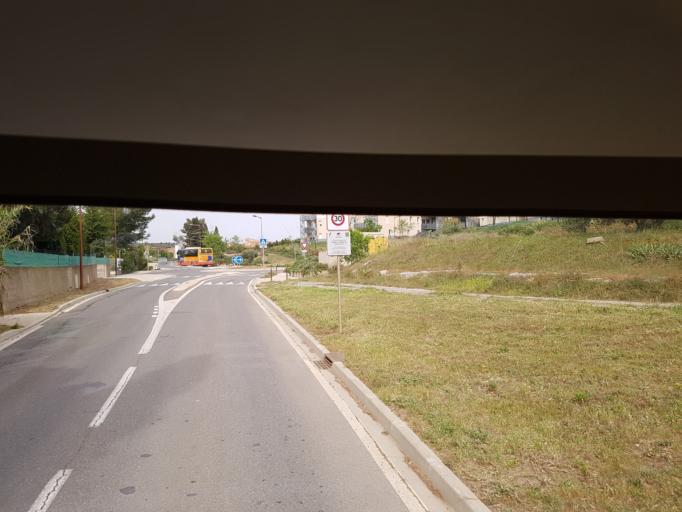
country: FR
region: Languedoc-Roussillon
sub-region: Departement de l'Herault
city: Lespignan
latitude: 43.2682
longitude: 3.1669
